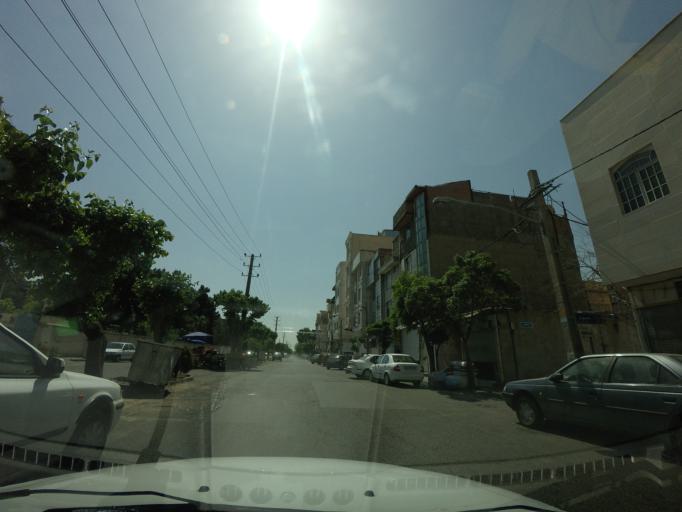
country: IR
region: Tehran
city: Tehran
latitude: 35.6386
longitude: 51.3665
